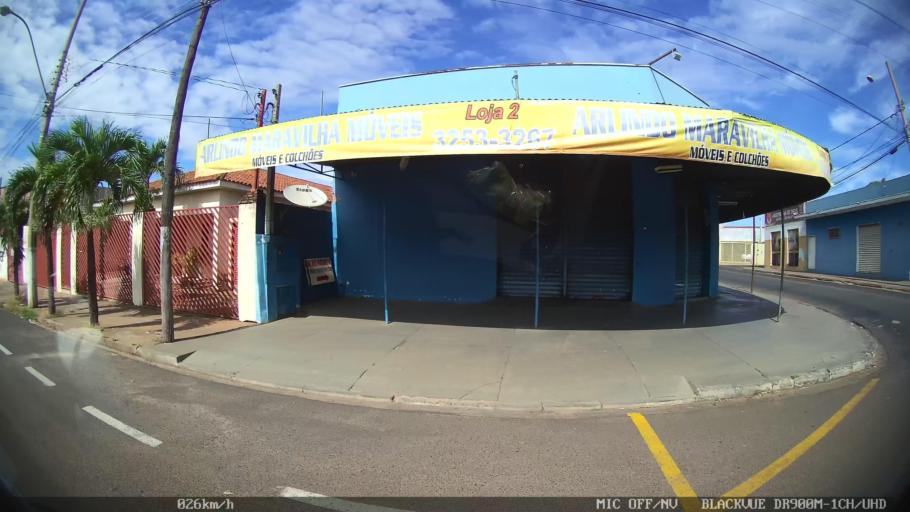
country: BR
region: Sao Paulo
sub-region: Bady Bassitt
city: Bady Bassitt
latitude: -20.8125
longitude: -49.5180
